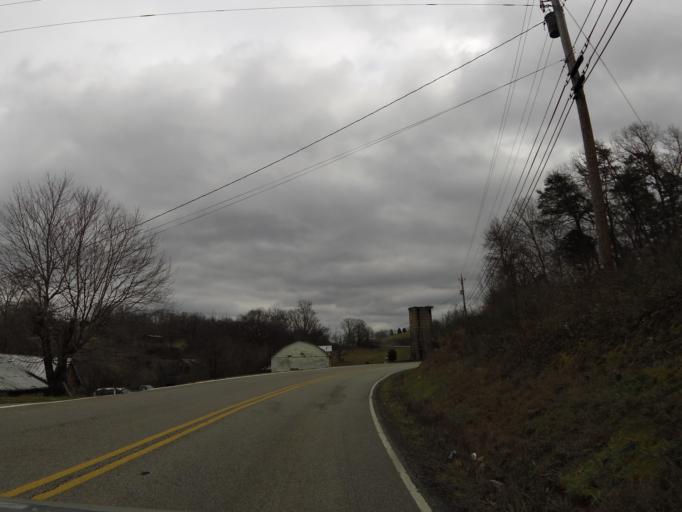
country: US
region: Tennessee
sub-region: Grainger County
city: Blaine
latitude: 36.1433
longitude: -83.6580
